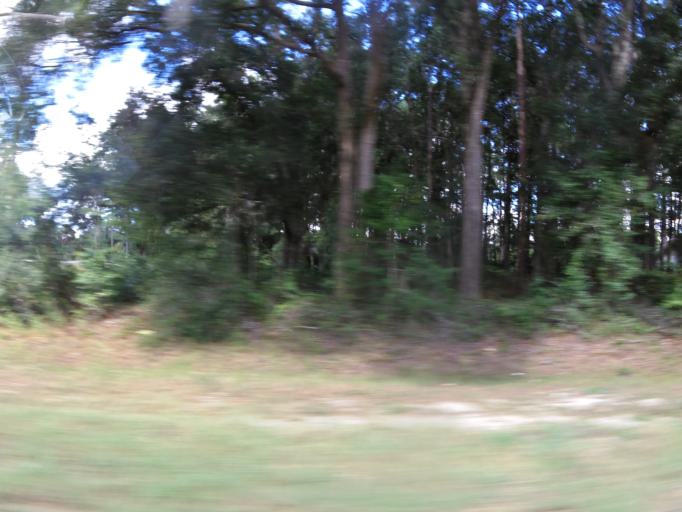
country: US
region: Georgia
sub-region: Echols County
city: Statenville
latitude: 30.7719
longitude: -83.1417
